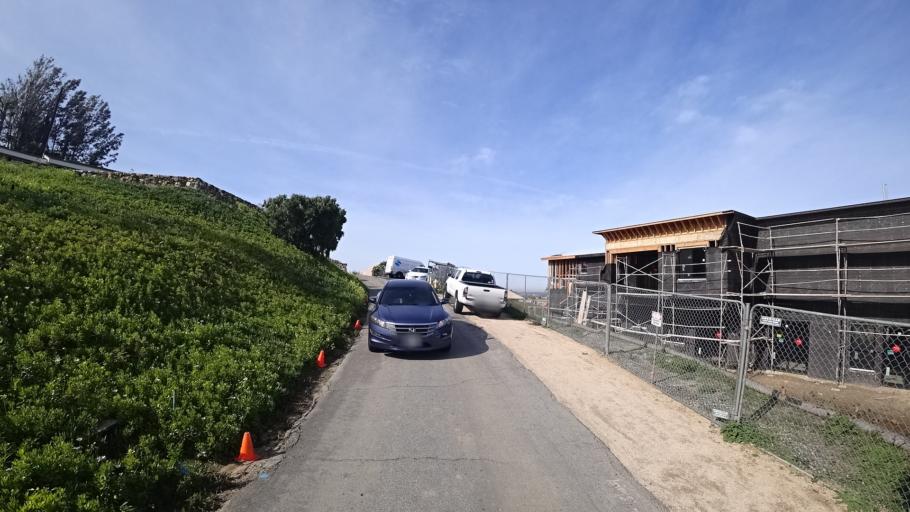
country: US
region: California
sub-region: Orange County
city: Yorba Linda
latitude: 33.8557
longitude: -117.7572
